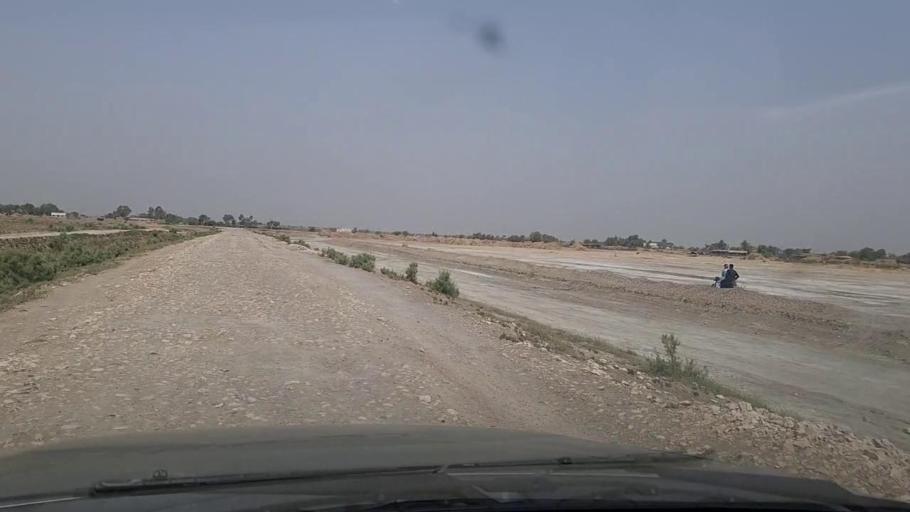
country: PK
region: Balochistan
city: Sohbatpur
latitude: 28.4137
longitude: 68.6921
